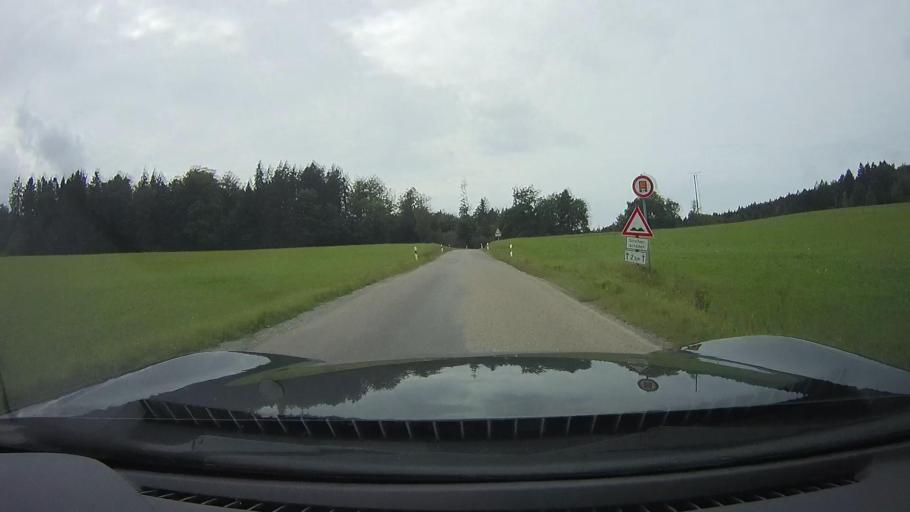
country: DE
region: Baden-Wuerttemberg
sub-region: Regierungsbezirk Stuttgart
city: Mainhardt
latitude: 49.0358
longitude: 9.5784
